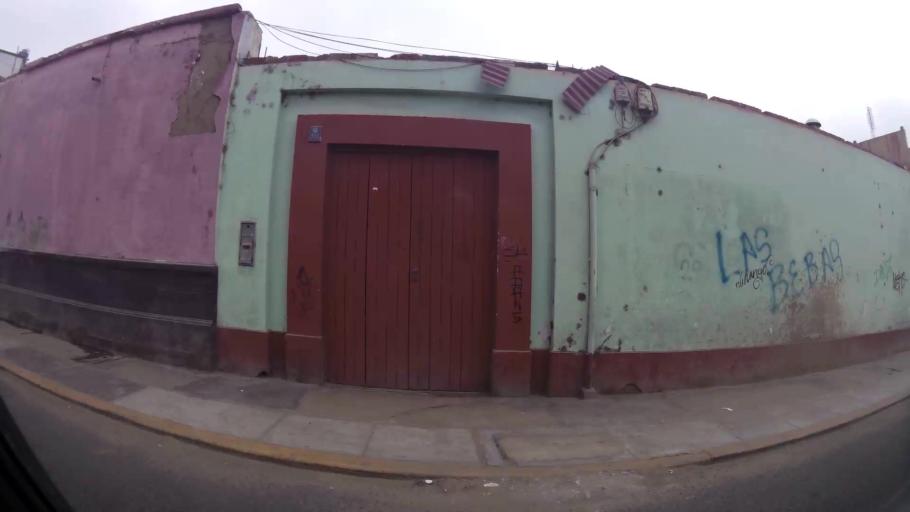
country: PE
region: La Libertad
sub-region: Provincia de Trujillo
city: Trujillo
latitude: -8.1140
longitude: -79.0309
